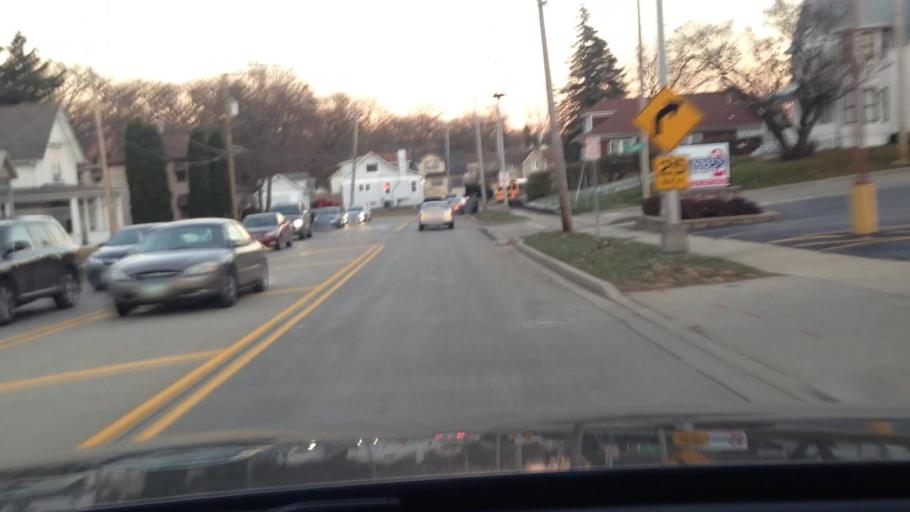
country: US
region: Illinois
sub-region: Kane County
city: Elgin
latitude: 42.0372
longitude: -88.2665
